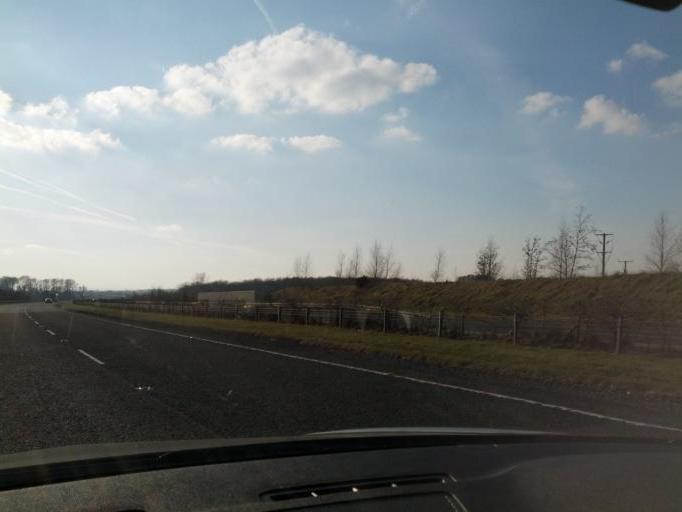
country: IE
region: Leinster
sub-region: Kildare
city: Monasterevin
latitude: 53.1138
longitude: -7.0589
